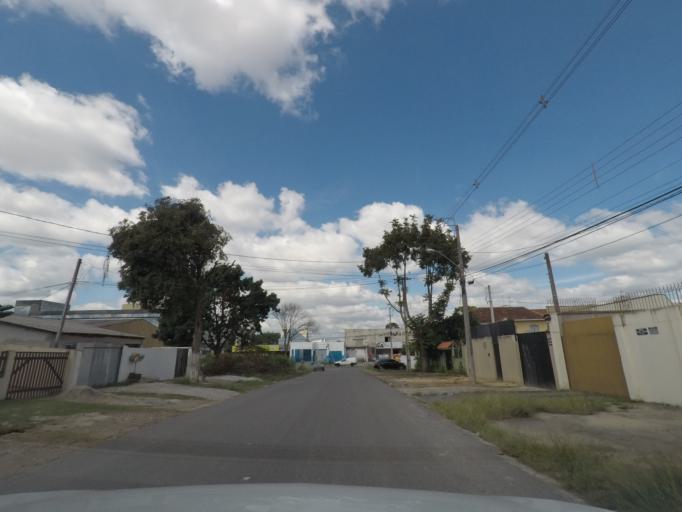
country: BR
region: Parana
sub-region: Sao Jose Dos Pinhais
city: Sao Jose dos Pinhais
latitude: -25.5010
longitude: -49.2223
